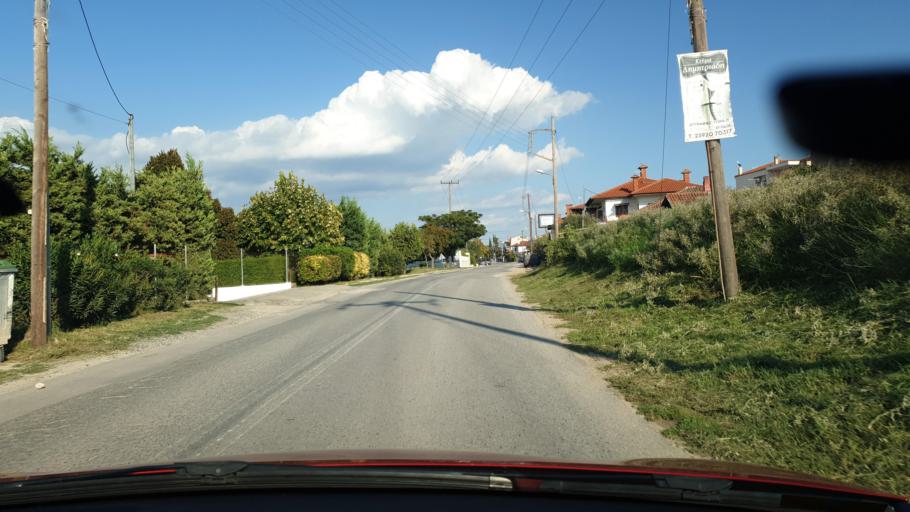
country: GR
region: Central Macedonia
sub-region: Nomos Thessalonikis
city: Agia Paraskevi
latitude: 40.4840
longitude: 23.0464
